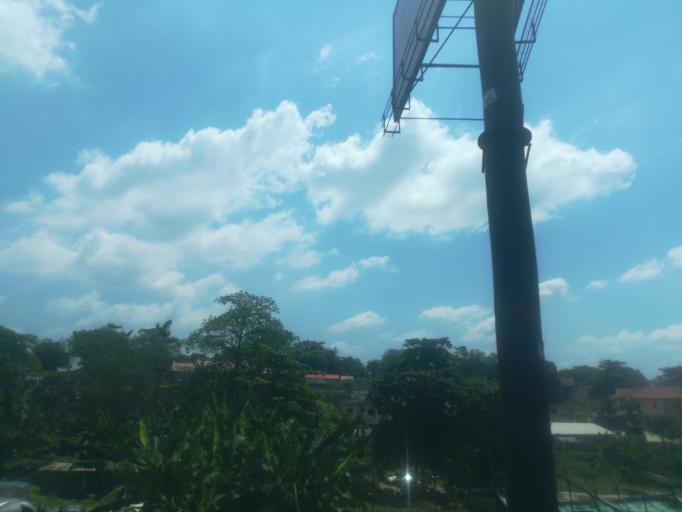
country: NG
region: Oyo
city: Ibadan
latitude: 7.3830
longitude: 3.8719
